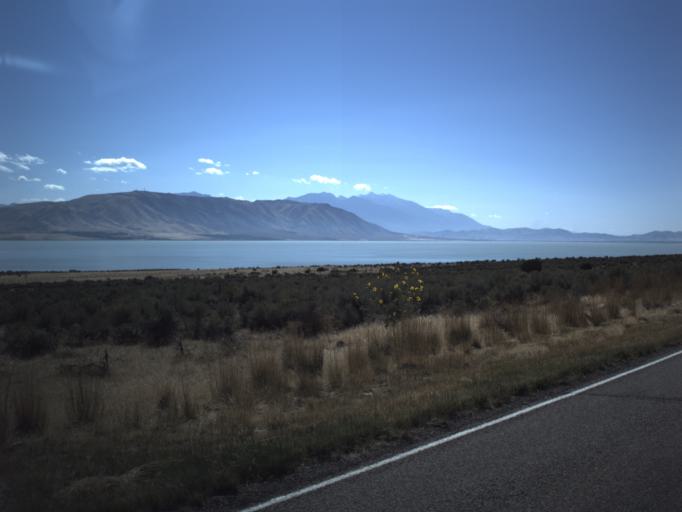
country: US
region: Utah
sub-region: Utah County
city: Saratoga Springs
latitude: 40.1956
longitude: -111.9044
